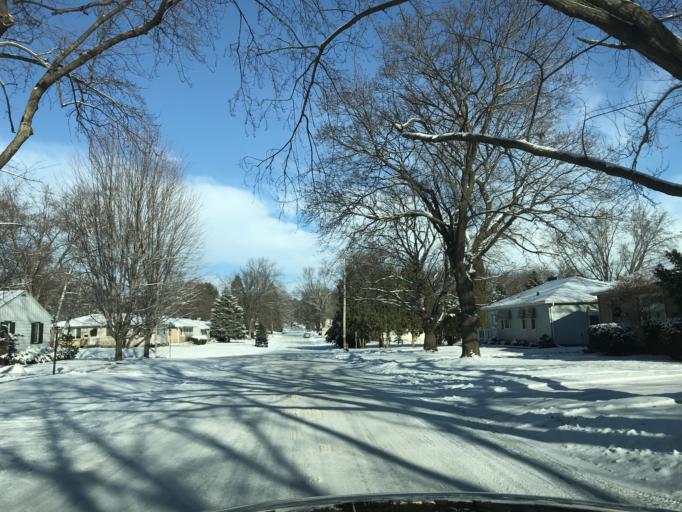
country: US
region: Wisconsin
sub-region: Dane County
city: Monona
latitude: 43.0749
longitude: -89.3118
